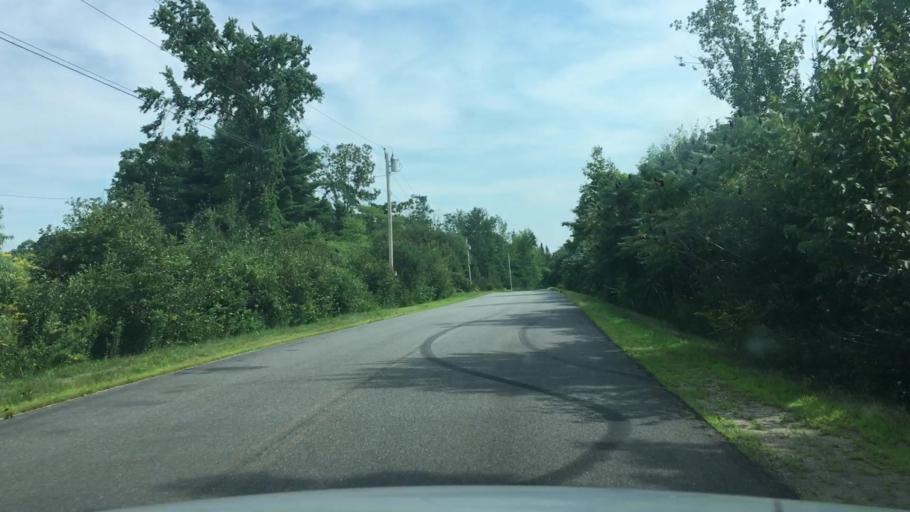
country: US
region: Maine
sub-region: Lincoln County
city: Jefferson
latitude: 44.2395
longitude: -69.4443
